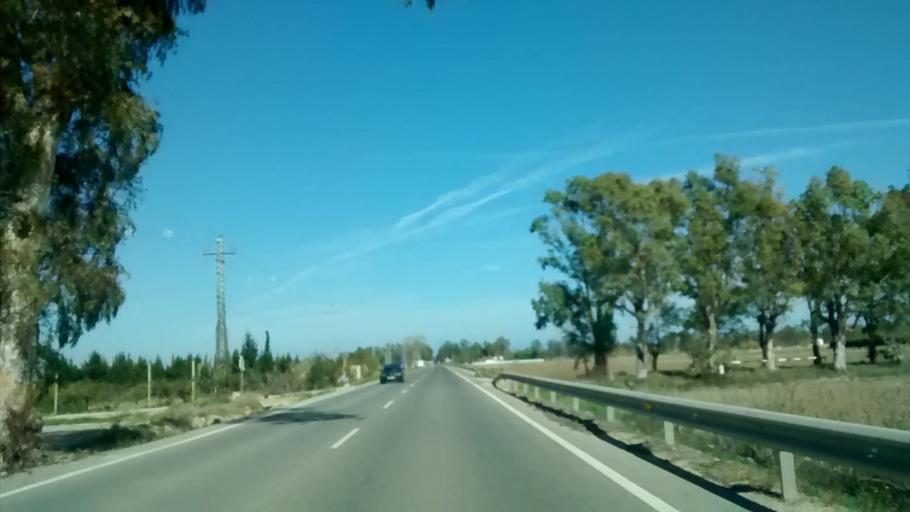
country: ES
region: Catalonia
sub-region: Provincia de Tarragona
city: Deltebre
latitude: 40.7124
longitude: 0.8209
